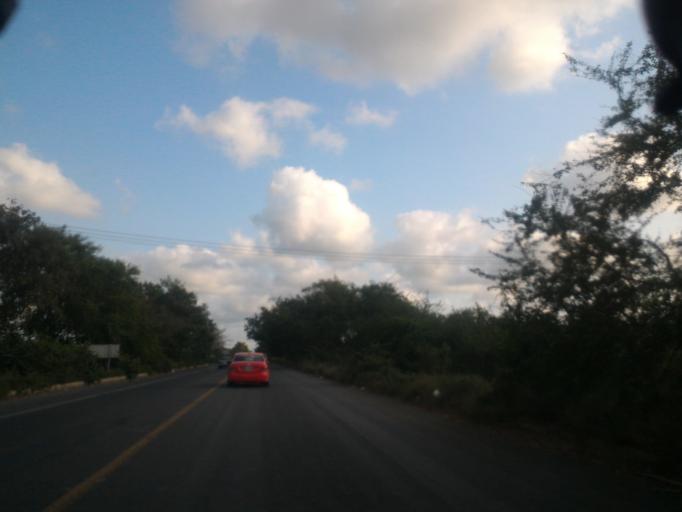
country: MX
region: Colima
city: Tecoman
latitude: 18.8625
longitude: -103.8365
